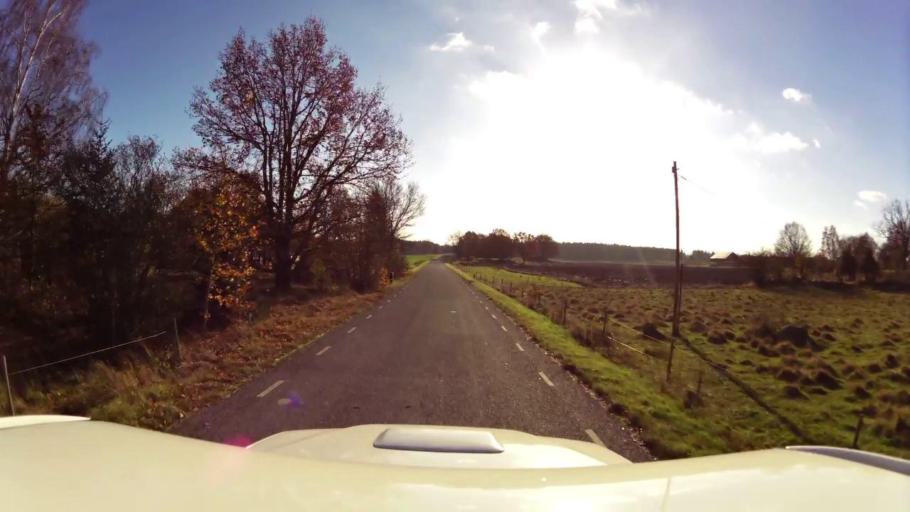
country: SE
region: OEstergoetland
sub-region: Linkopings Kommun
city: Linghem
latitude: 58.4765
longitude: 15.7590
